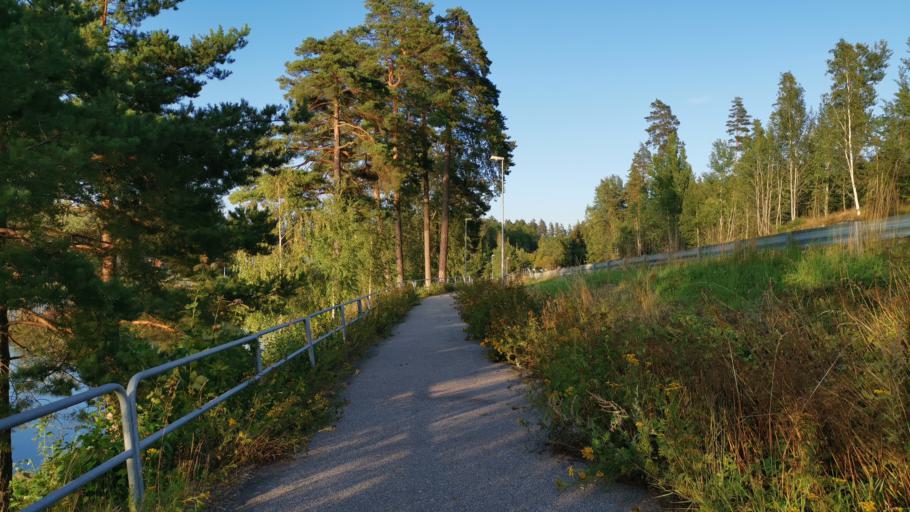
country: SE
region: OEstergoetland
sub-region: Norrkopings Kommun
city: Krokek
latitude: 58.7268
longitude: 16.4325
